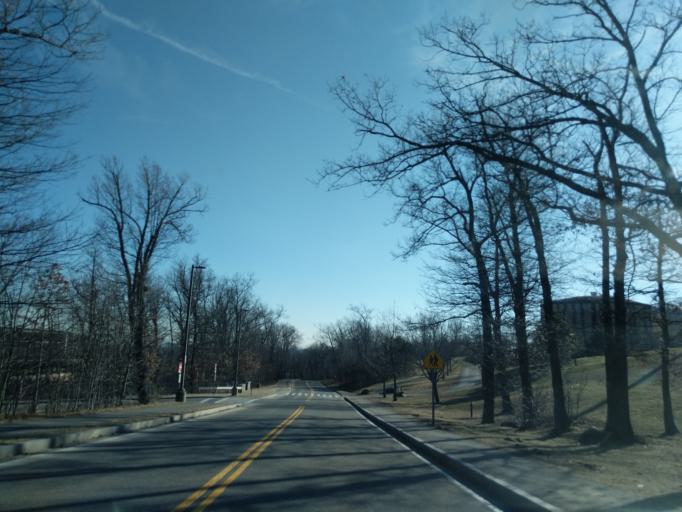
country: US
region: Massachusetts
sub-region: Worcester County
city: Hamilton
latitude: 42.2781
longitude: -71.7794
